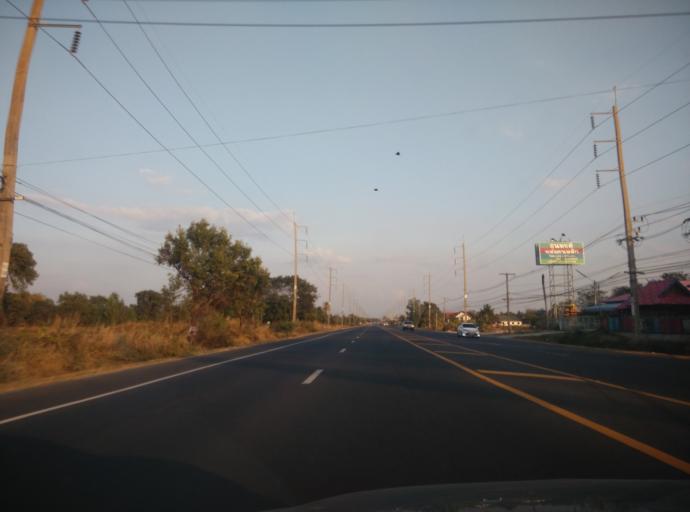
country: TH
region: Sisaket
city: Uthumphon Phisai
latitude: 15.1566
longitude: 104.1844
